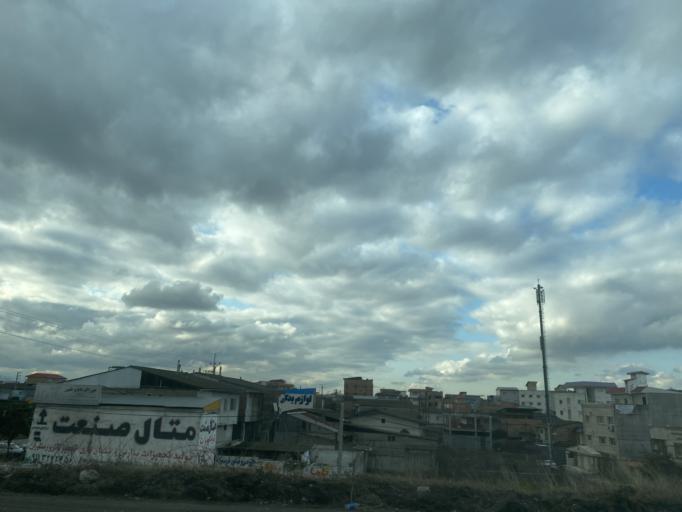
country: IR
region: Mazandaran
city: Amol
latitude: 36.4516
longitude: 52.3949
